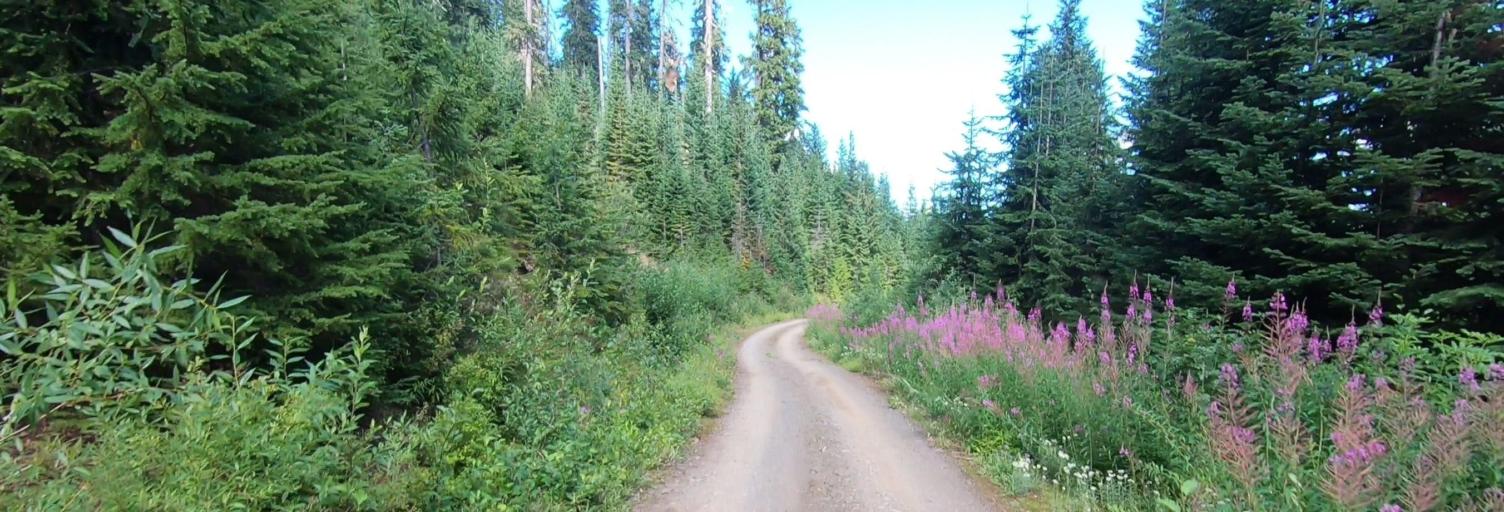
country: CA
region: British Columbia
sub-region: Fraser Valley Regional District
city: Chilliwack
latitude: 48.8743
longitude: -121.8001
